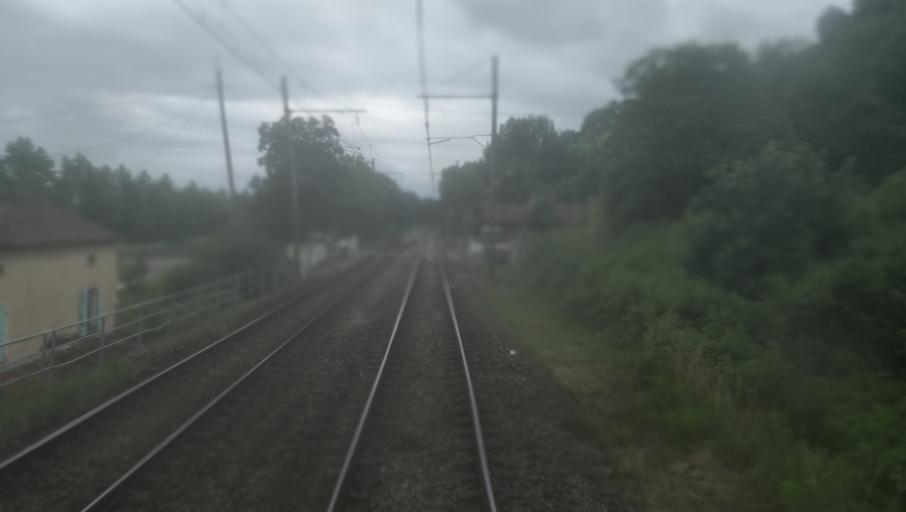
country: FR
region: Midi-Pyrenees
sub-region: Departement du Tarn-et-Garonne
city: Saint-Nicolas-de-la-Grave
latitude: 44.0937
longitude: 1.0512
